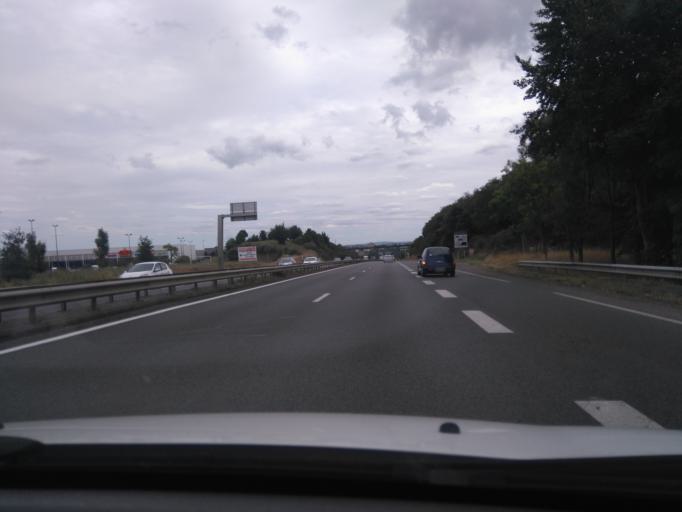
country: FR
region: Brittany
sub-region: Departement des Cotes-d'Armor
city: Saint-Brieuc
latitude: 48.5321
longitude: -2.7571
